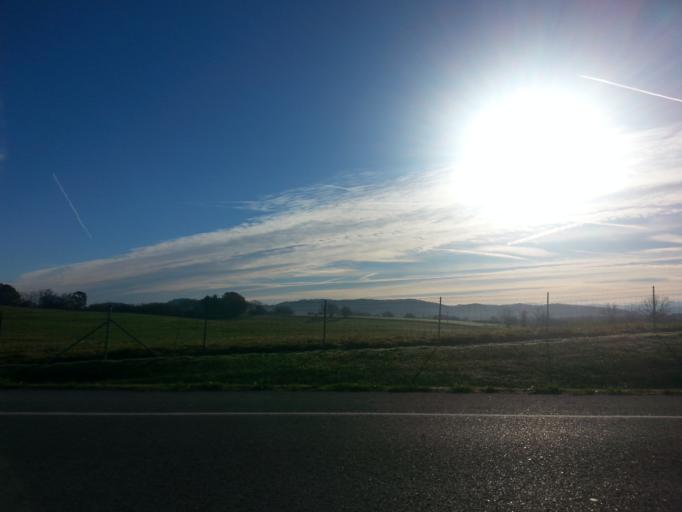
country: US
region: Tennessee
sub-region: Blount County
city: Alcoa
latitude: 35.8470
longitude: -83.9641
